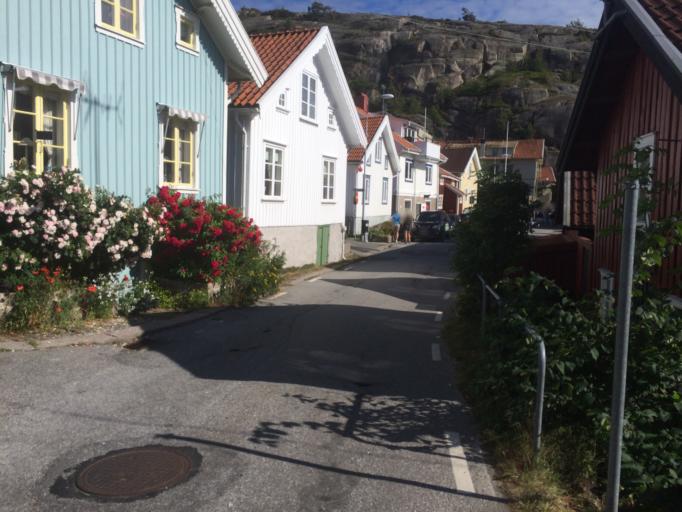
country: SE
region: Vaestra Goetaland
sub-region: Tanums Kommun
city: Grebbestad
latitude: 58.5992
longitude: 11.2820
